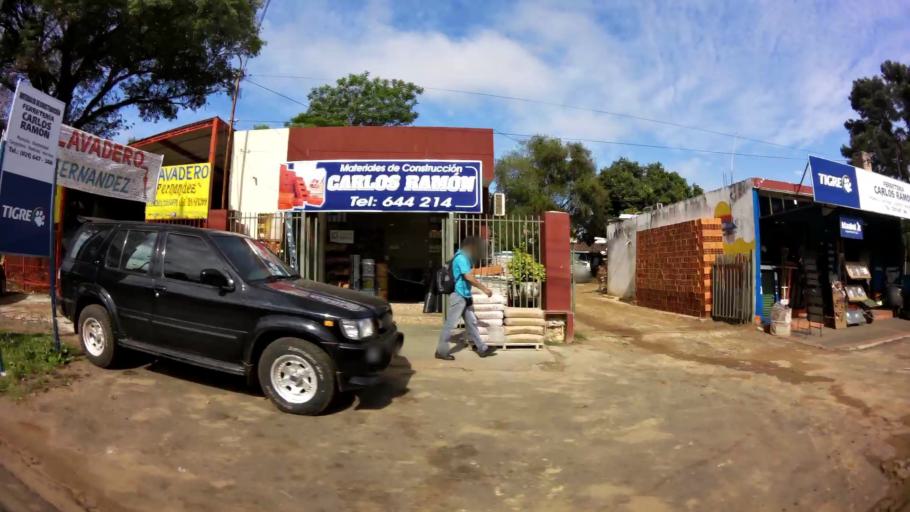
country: PY
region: Central
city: San Lorenzo
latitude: -25.2748
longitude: -57.4863
